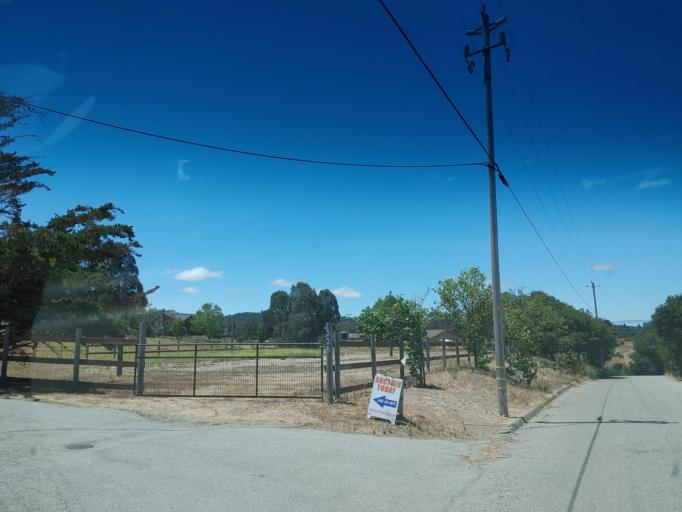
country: US
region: California
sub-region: San Benito County
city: Aromas
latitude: 36.8625
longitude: -121.6301
